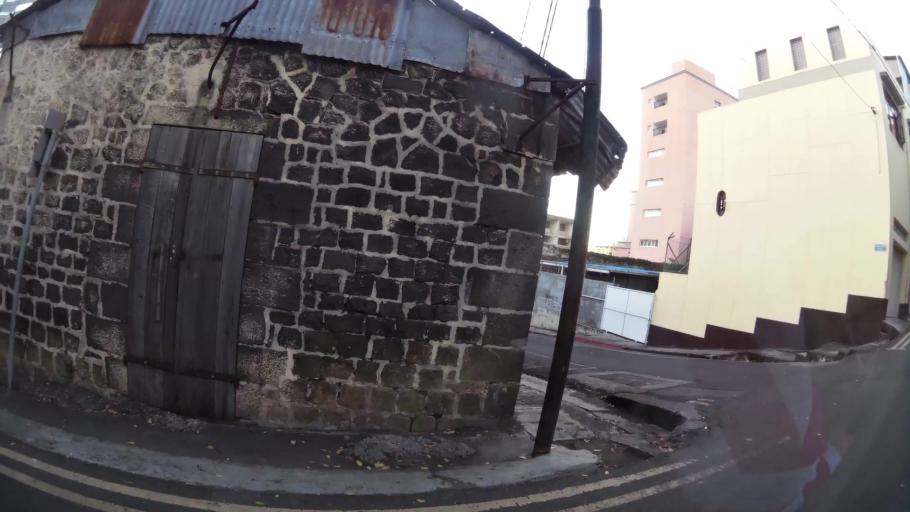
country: MU
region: Port Louis
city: Port Louis
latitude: -20.1628
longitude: 57.5079
